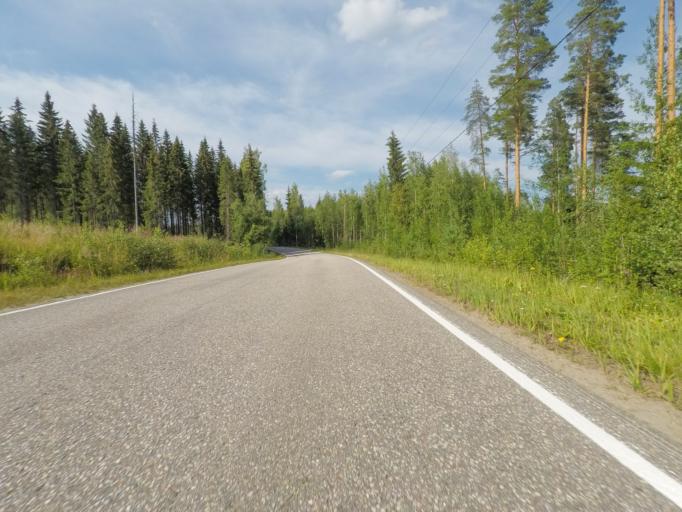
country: FI
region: Southern Savonia
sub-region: Savonlinna
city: Sulkava
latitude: 61.7767
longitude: 28.2394
